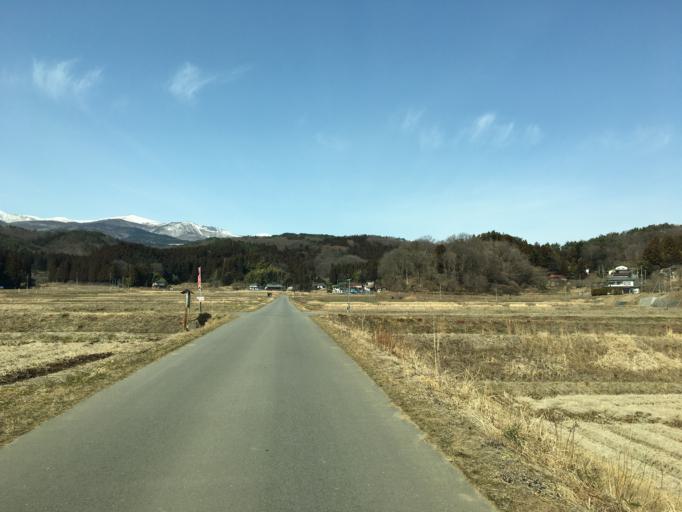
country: JP
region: Fukushima
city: Nihommatsu
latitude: 37.5854
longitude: 140.3819
